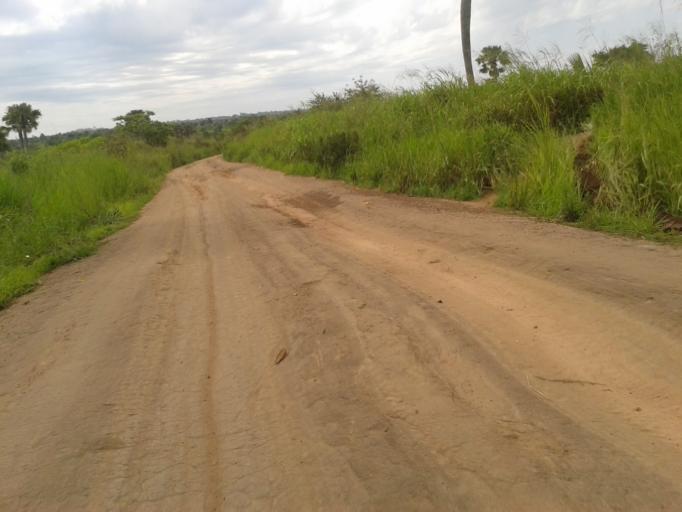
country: UG
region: Northern Region
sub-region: Gulu District
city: Gulu
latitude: 2.8276
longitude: 32.2543
